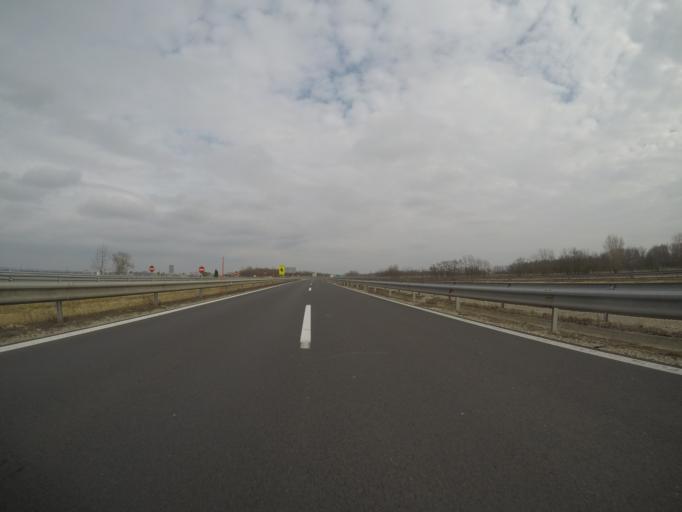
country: SI
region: Murska Sobota
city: Bakovci
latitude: 46.6355
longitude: 16.1675
